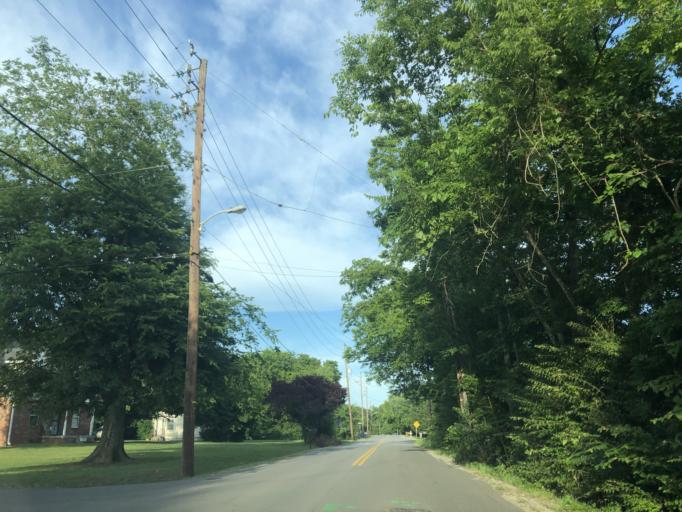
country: US
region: Tennessee
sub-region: Davidson County
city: Nashville
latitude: 36.2097
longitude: -86.8463
